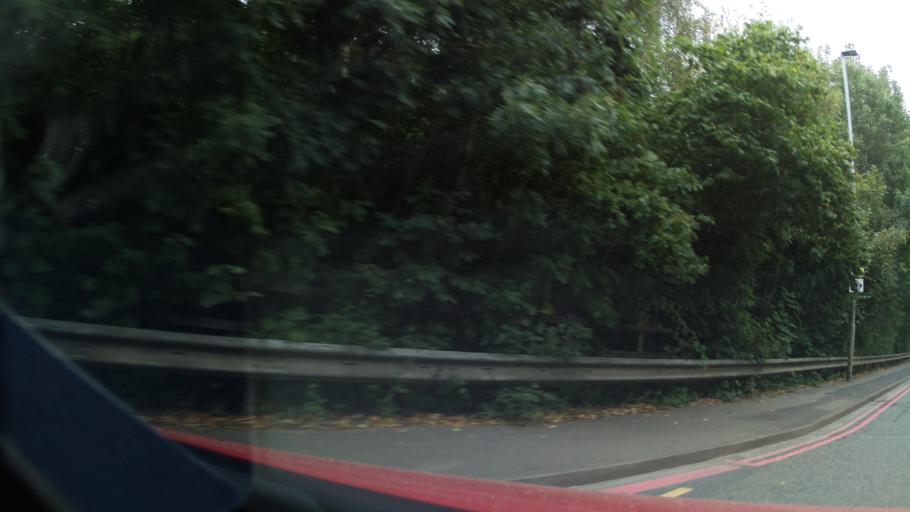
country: GB
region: England
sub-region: Stoke-on-Trent
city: Stoke-on-Trent
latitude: 53.0047
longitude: -2.1774
